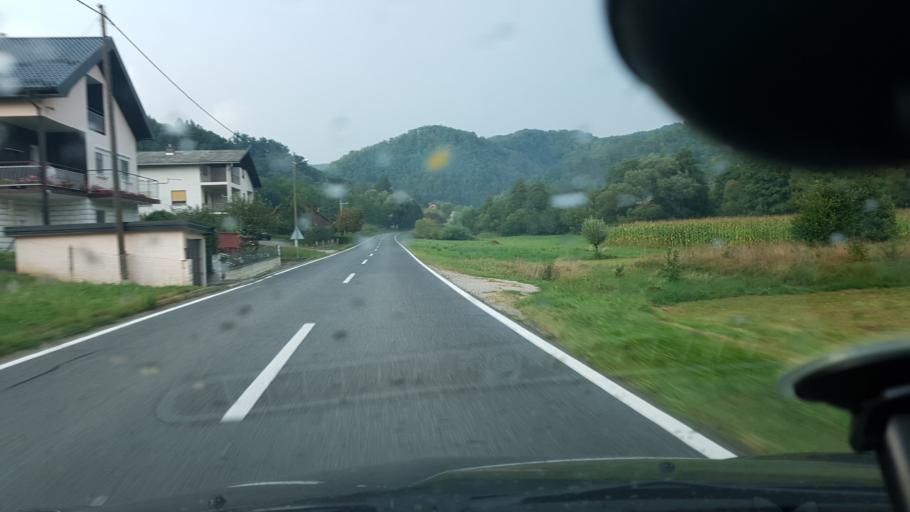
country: HR
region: Krapinsko-Zagorska
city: Pregrada
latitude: 46.2121
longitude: 15.7498
